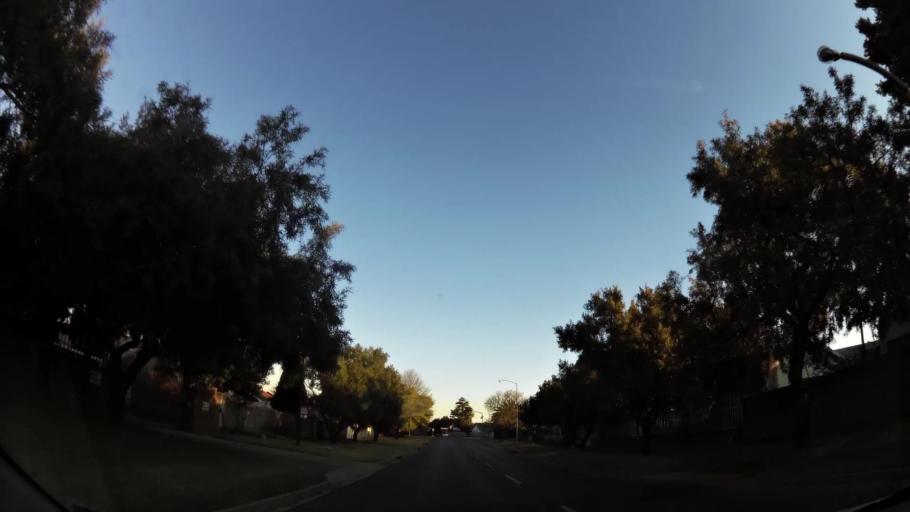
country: ZA
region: Gauteng
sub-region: City of Johannesburg Metropolitan Municipality
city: Roodepoort
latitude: -26.1517
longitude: 27.8908
